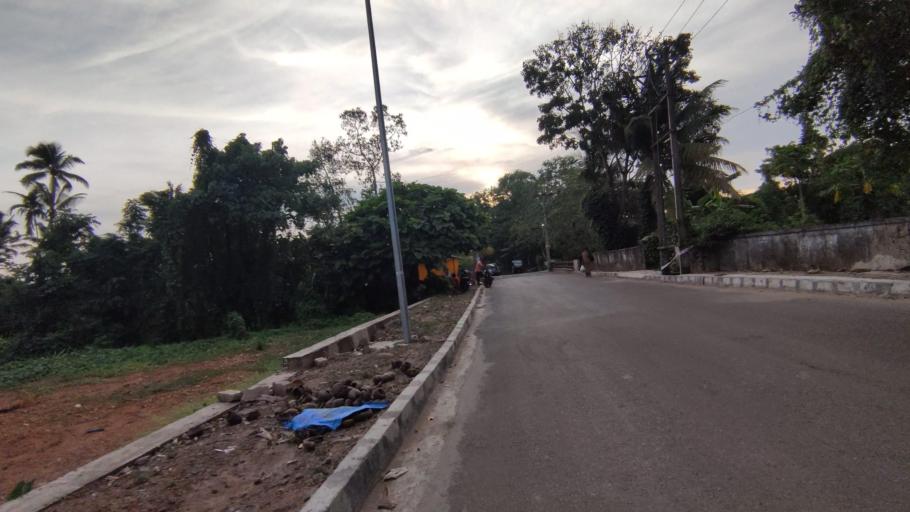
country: IN
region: Kerala
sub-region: Kottayam
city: Kottayam
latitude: 9.6435
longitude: 76.5159
